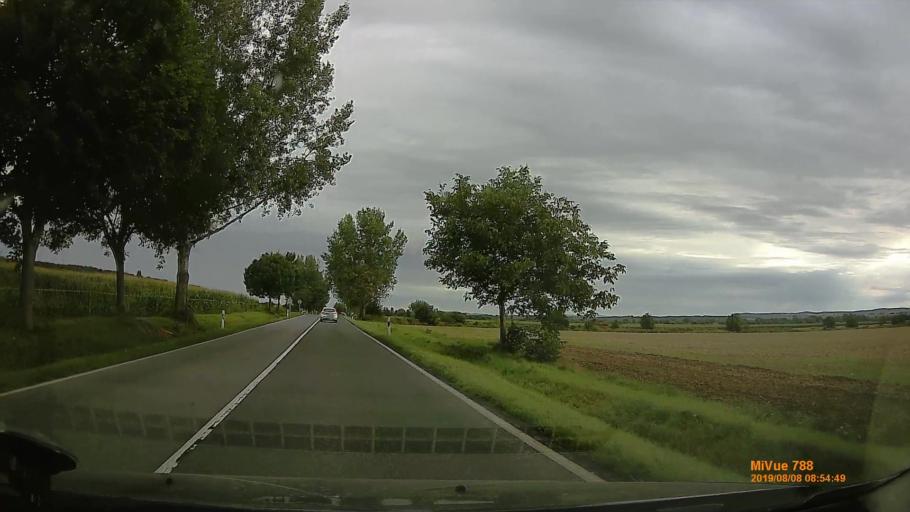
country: HU
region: Zala
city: Pacsa
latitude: 46.6182
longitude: 16.9204
